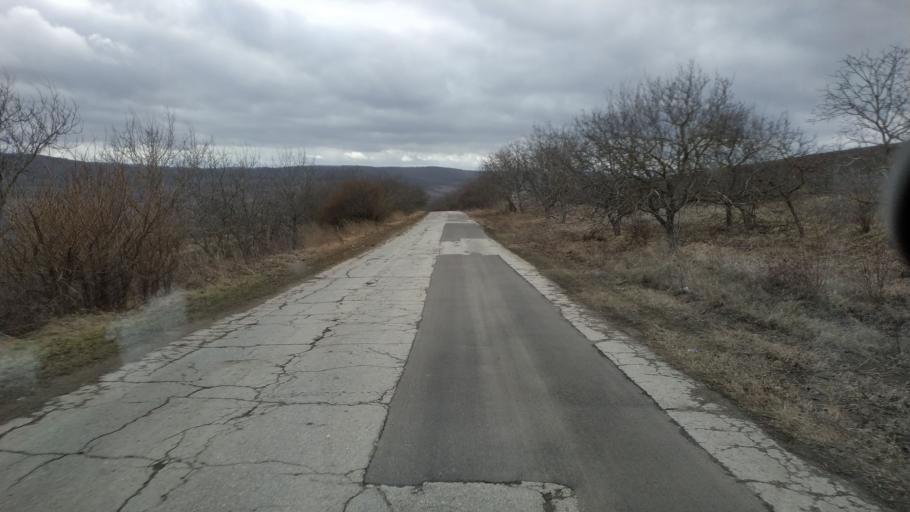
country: MD
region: Stinga Nistrului
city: Bucovat
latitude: 47.2220
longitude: 28.4167
